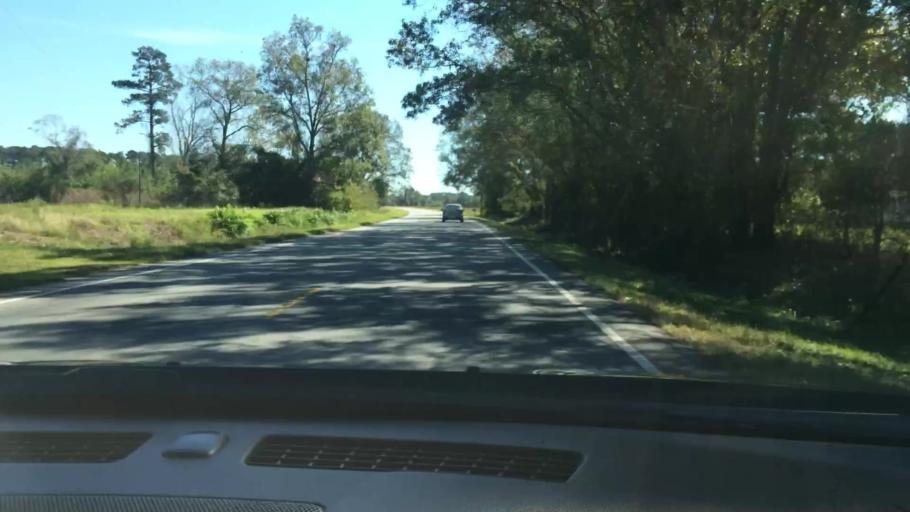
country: US
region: North Carolina
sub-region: Pitt County
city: Grifton
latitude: 35.3539
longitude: -77.3366
